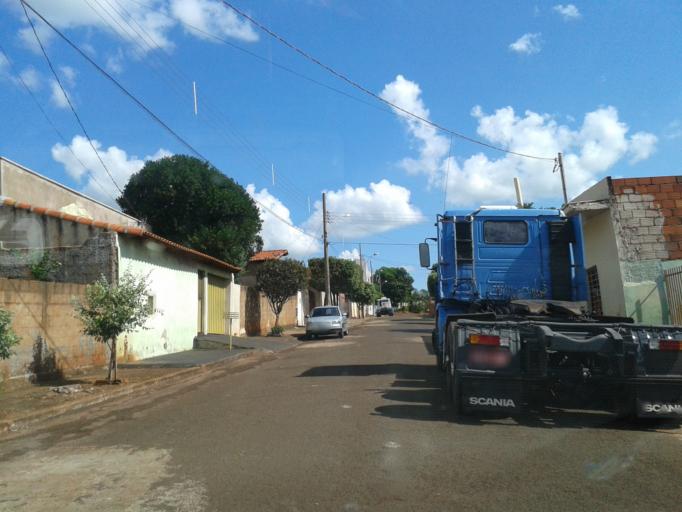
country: BR
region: Minas Gerais
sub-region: Capinopolis
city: Capinopolis
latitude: -18.6856
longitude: -49.5763
